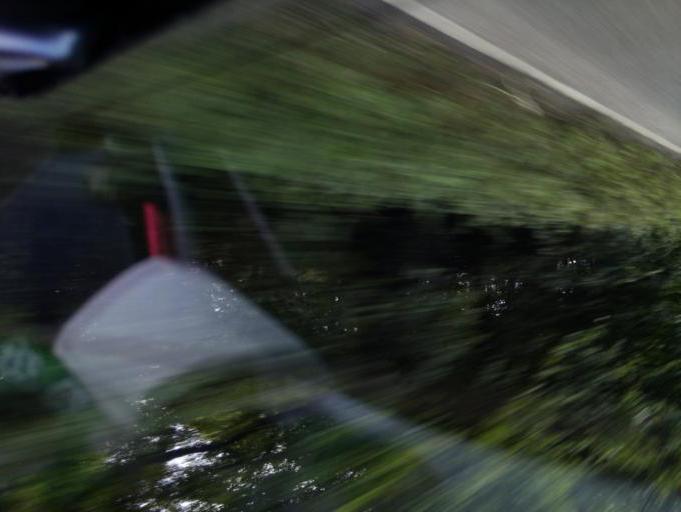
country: GB
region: England
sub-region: Devon
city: Honiton
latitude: 50.7520
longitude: -3.2095
